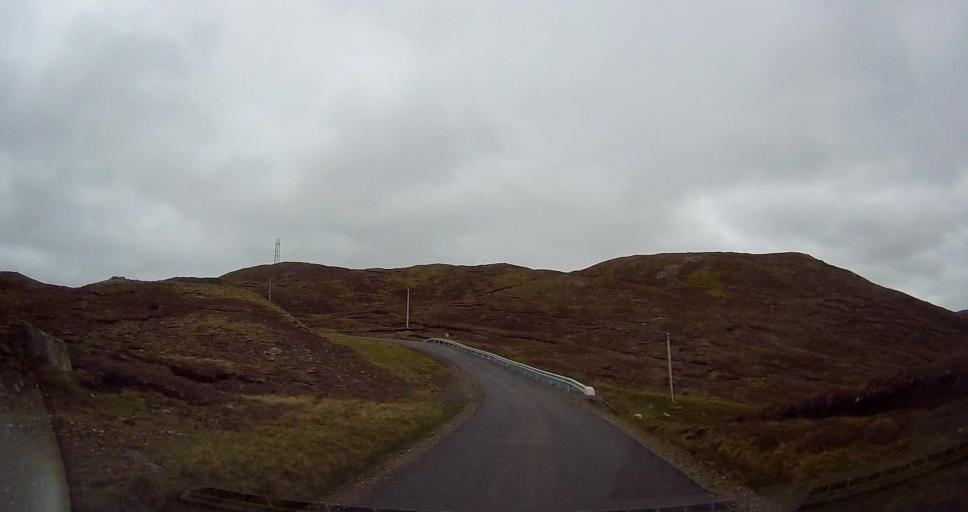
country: GB
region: Scotland
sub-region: Shetland Islands
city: Lerwick
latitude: 60.3407
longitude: -1.3095
